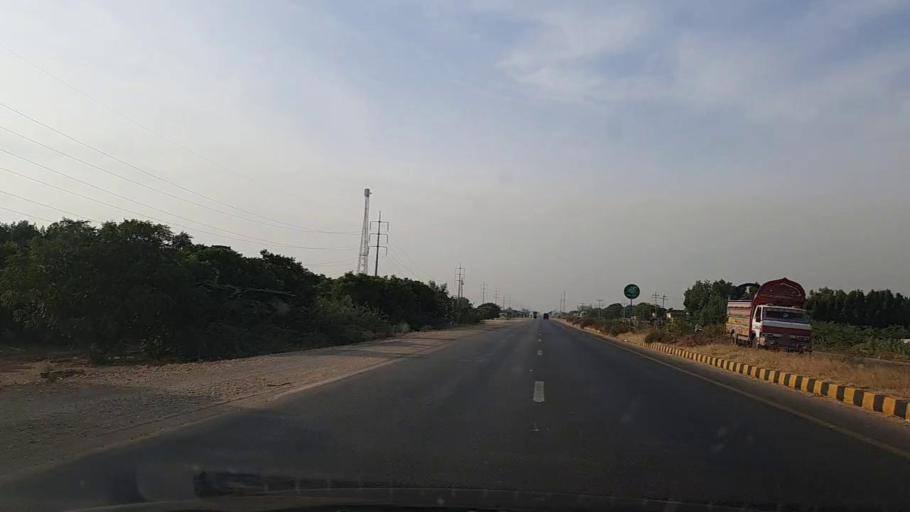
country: PK
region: Sindh
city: Gharo
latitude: 24.7791
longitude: 67.5381
